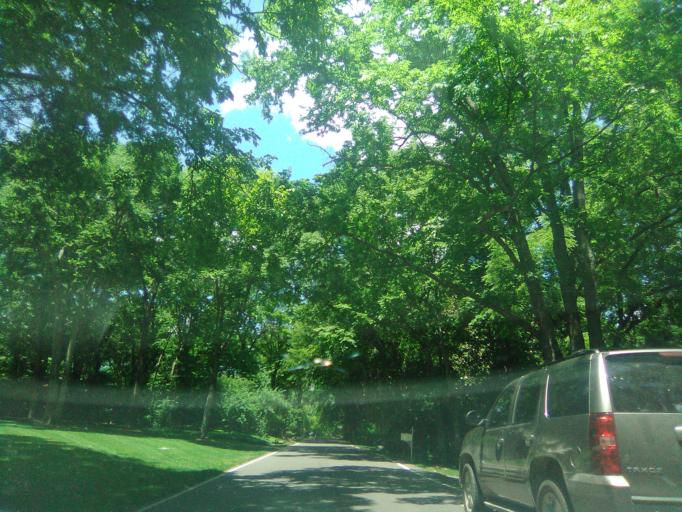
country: US
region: Tennessee
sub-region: Davidson County
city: Belle Meade
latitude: 36.1122
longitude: -86.8503
